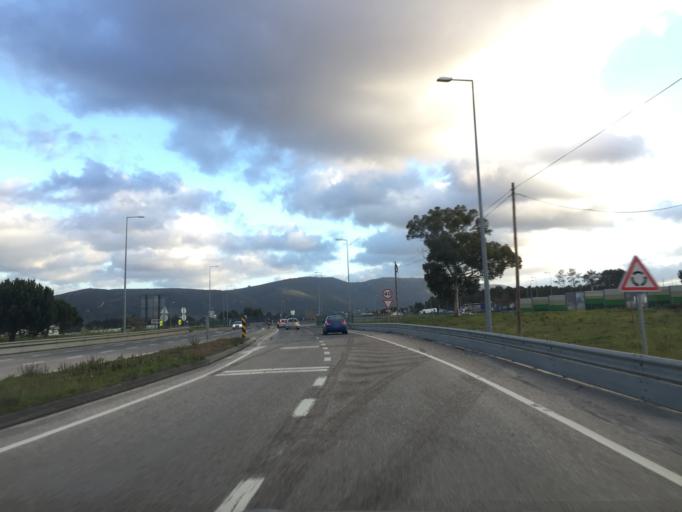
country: PT
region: Leiria
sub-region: Porto de Mos
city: Porto de Mos
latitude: 39.6216
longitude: -8.8575
